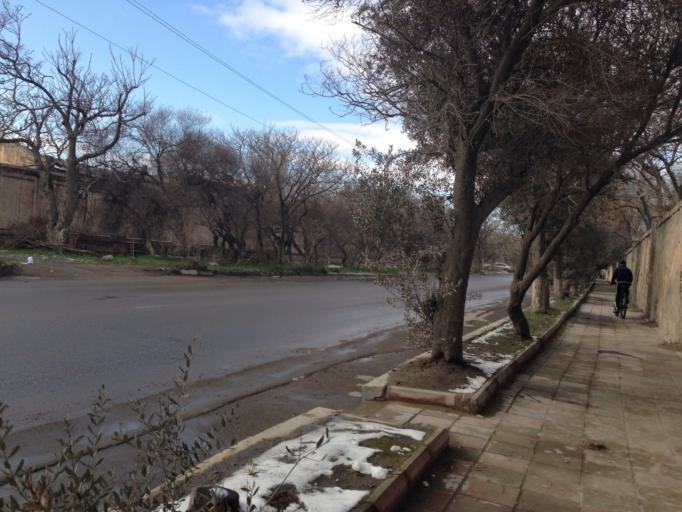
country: AZ
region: Baki
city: Baku
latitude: 40.3984
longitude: 49.8909
